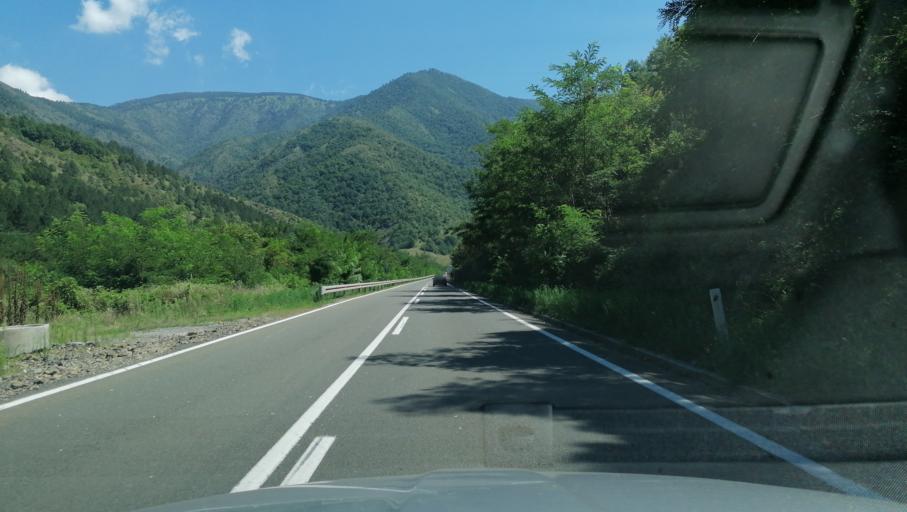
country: RS
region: Central Serbia
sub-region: Raski Okrug
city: Kraljevo
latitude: 43.5955
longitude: 20.5616
